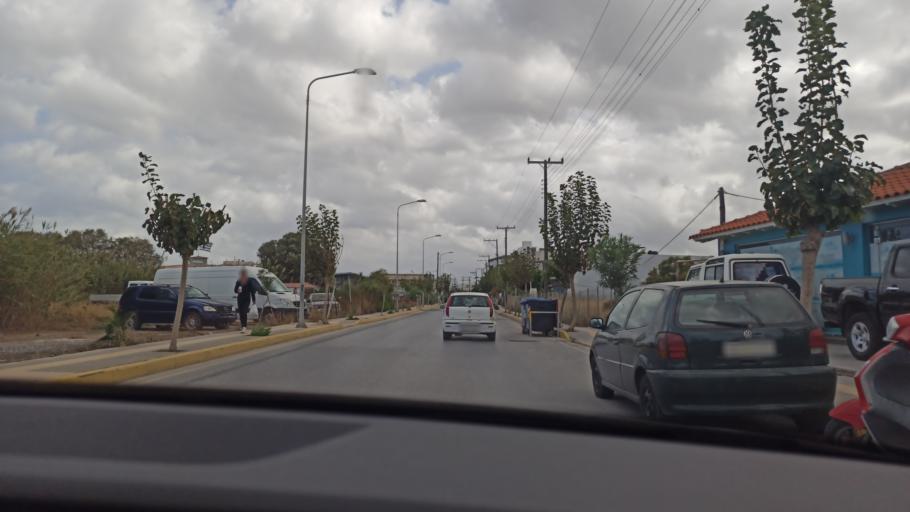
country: GR
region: Crete
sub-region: Nomos Irakleiou
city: Gazi
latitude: 35.3346
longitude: 25.0932
